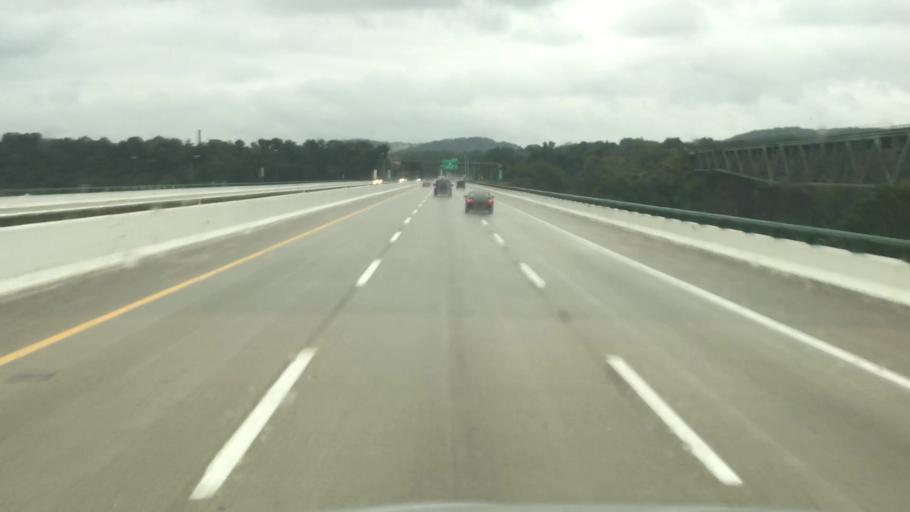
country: US
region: Pennsylvania
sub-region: Allegheny County
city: Cheswick
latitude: 40.5365
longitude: -79.8223
